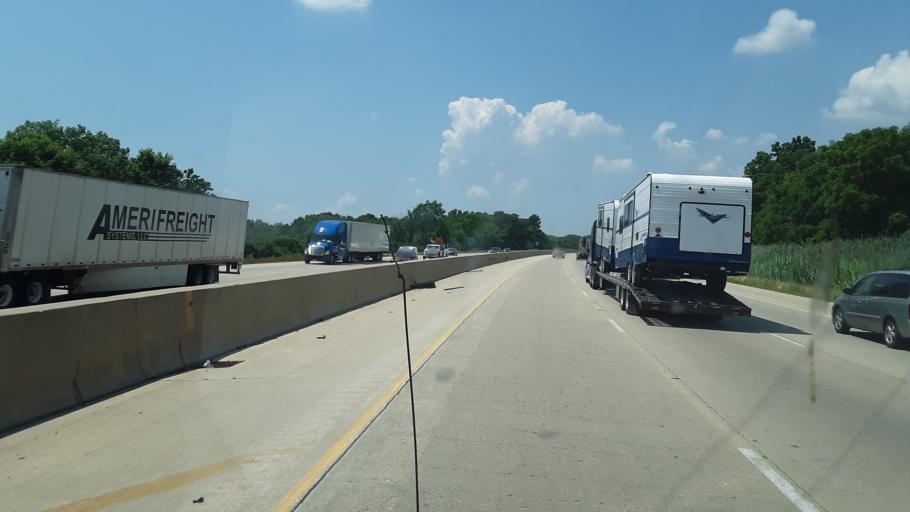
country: US
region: Illinois
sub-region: Will County
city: Mokena
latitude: 41.5476
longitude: -87.9226
